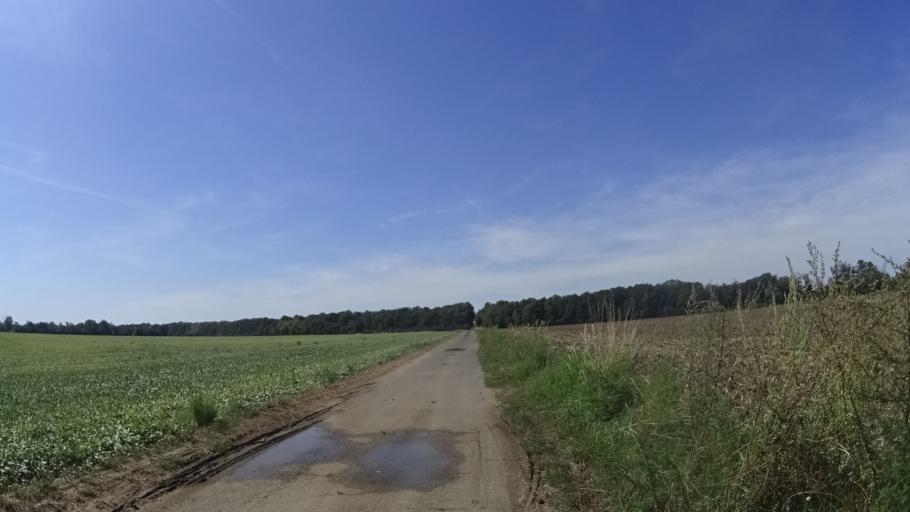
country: AT
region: Lower Austria
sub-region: Politischer Bezirk Ganserndorf
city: Angern an der March
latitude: 48.3676
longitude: 16.8633
